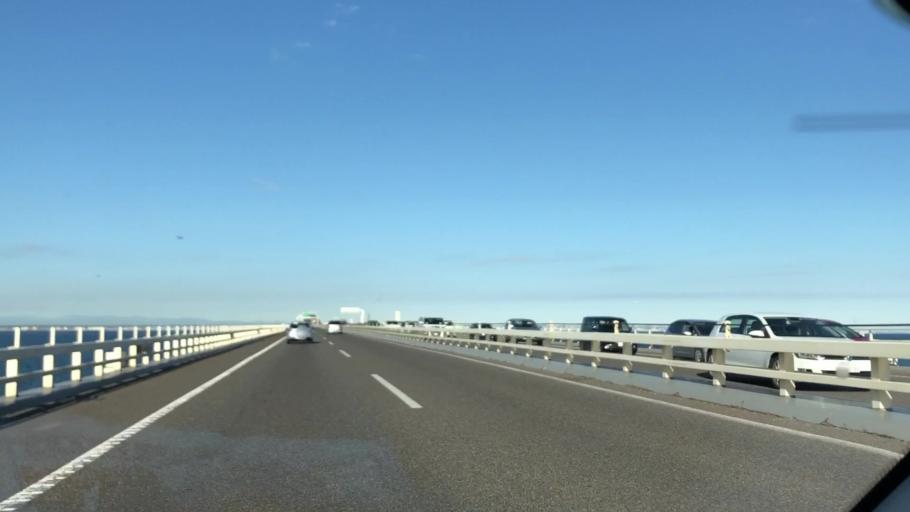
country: JP
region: Chiba
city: Kisarazu
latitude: 35.4451
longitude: 139.9026
